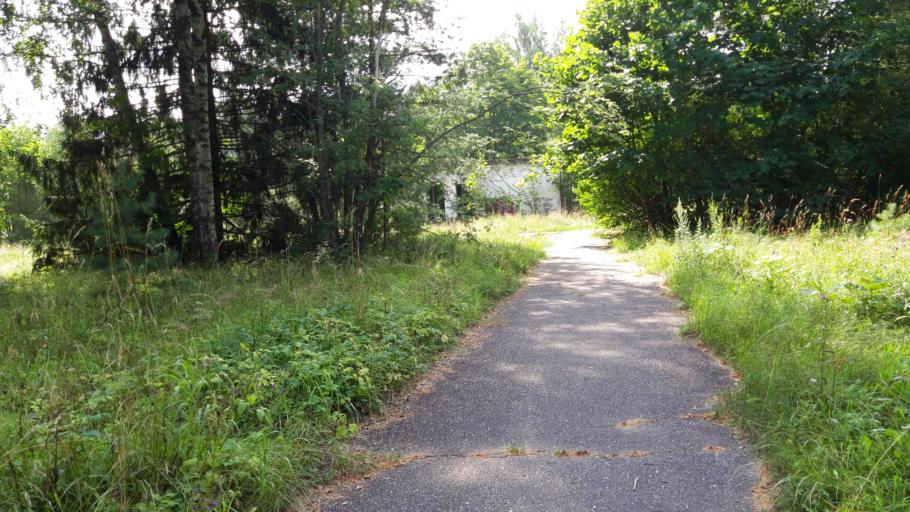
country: RU
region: Tverskaya
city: Konakovo
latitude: 56.6666
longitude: 36.6821
